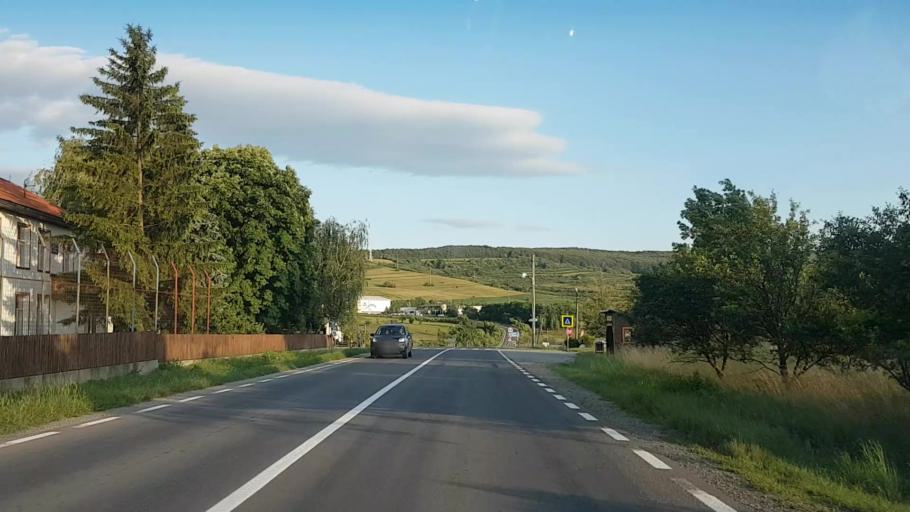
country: RO
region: Harghita
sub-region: Comuna Lupeni
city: Lupeni
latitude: 46.3605
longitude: 25.2380
